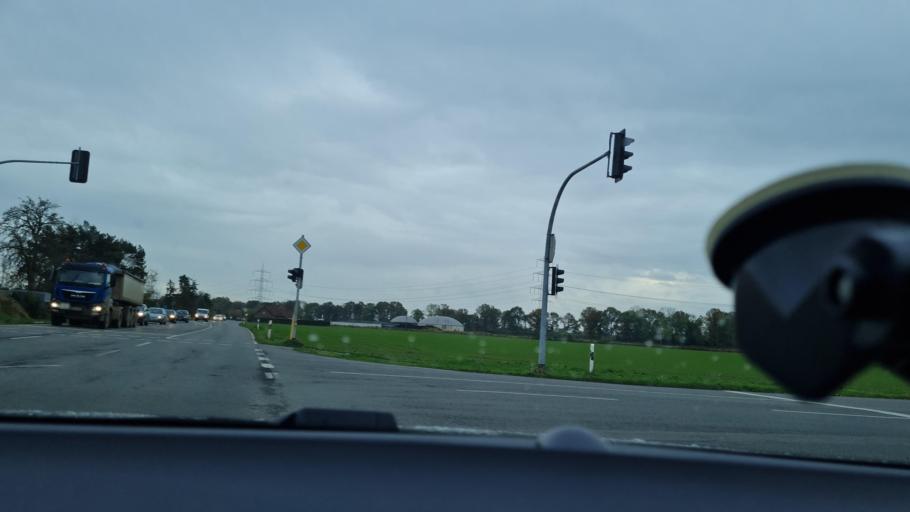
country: DE
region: North Rhine-Westphalia
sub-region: Regierungsbezirk Dusseldorf
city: Voerde
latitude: 51.6094
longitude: 6.6520
